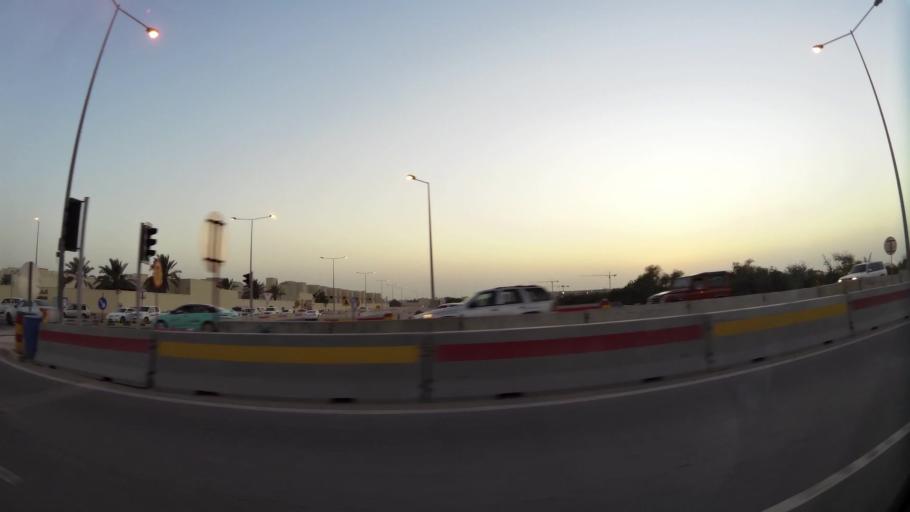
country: QA
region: Baladiyat ar Rayyan
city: Ar Rayyan
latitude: 25.3106
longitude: 51.4618
